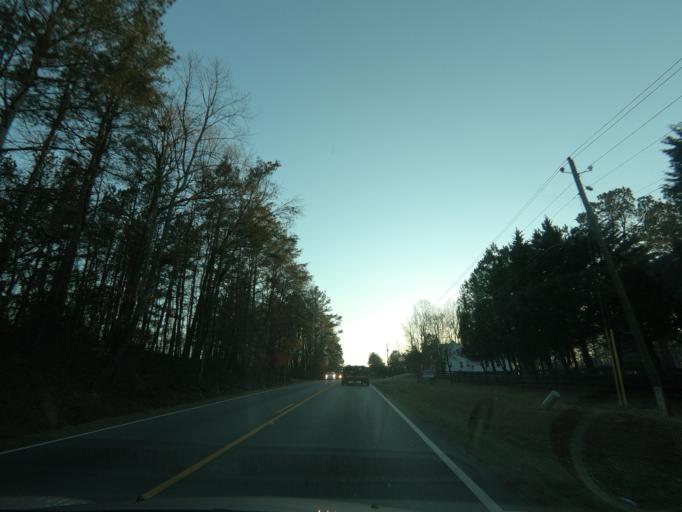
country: US
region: Georgia
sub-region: Cherokee County
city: Ball Ground
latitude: 34.2846
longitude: -84.2899
